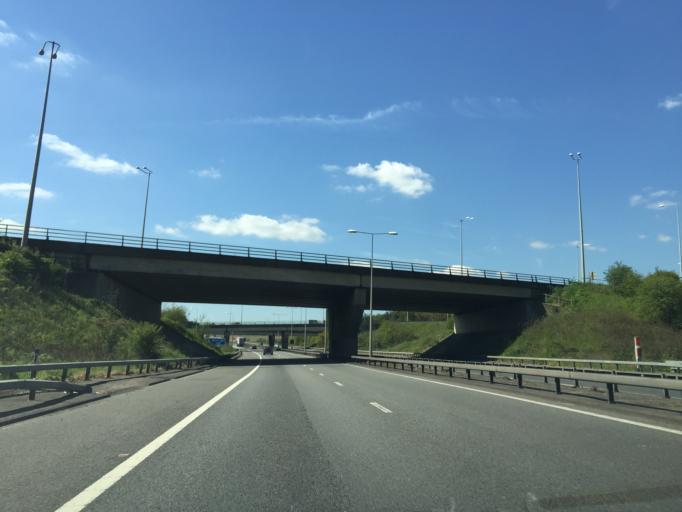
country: GB
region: England
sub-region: Essex
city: Epping
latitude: 51.6800
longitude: 0.1258
